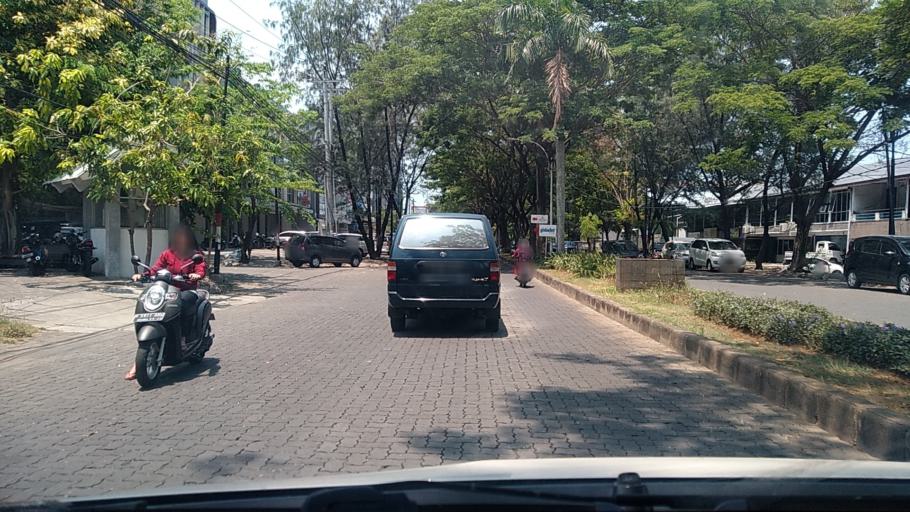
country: ID
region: Central Java
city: Semarang
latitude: -6.9647
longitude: 110.3906
